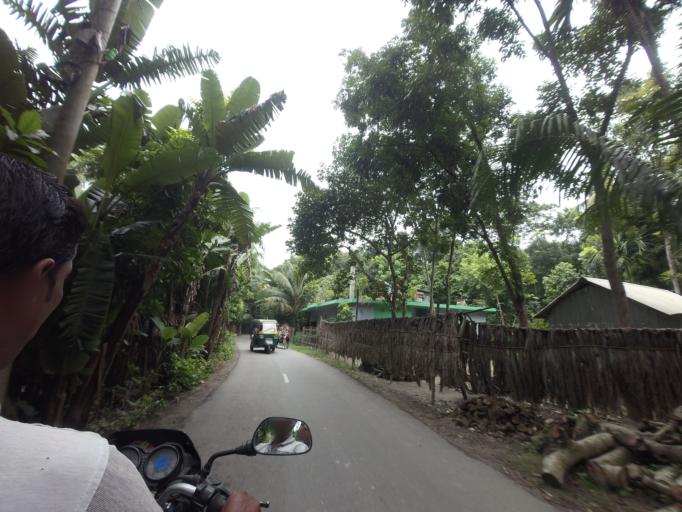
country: BD
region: Khulna
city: Kalia
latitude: 23.1317
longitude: 89.6424
